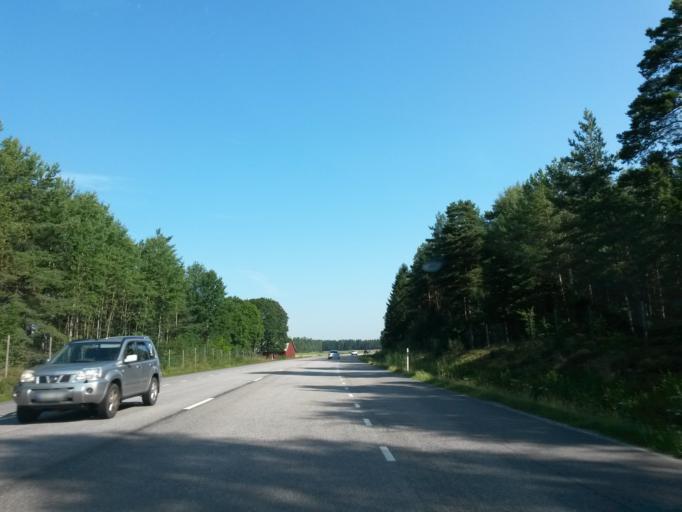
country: SE
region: Vaestra Goetaland
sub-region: Vara Kommun
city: Vara
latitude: 58.1956
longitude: 12.8987
